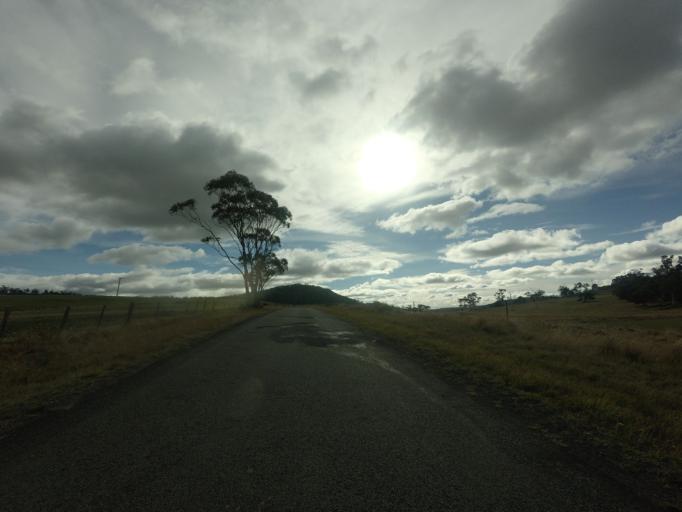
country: AU
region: Tasmania
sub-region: Brighton
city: Bridgewater
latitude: -42.3953
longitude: 147.3683
